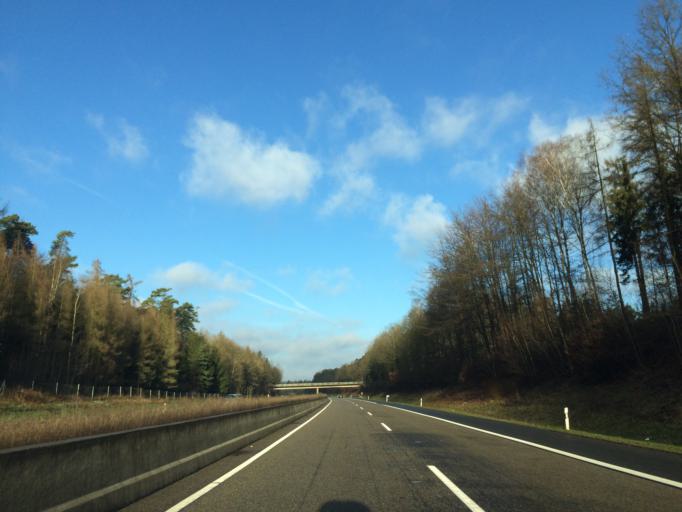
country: DE
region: Hesse
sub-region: Regierungsbezirk Kassel
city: Niederaula
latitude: 50.7363
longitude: 9.6432
